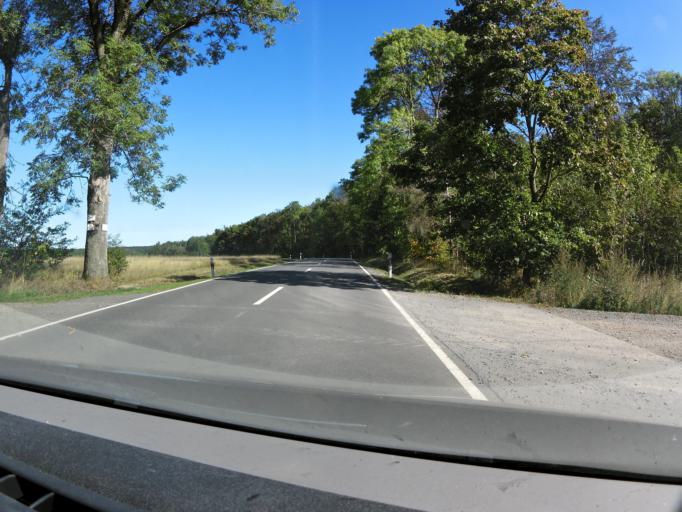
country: DE
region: Saxony-Anhalt
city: Hasselfelde
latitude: 51.6739
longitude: 10.8977
